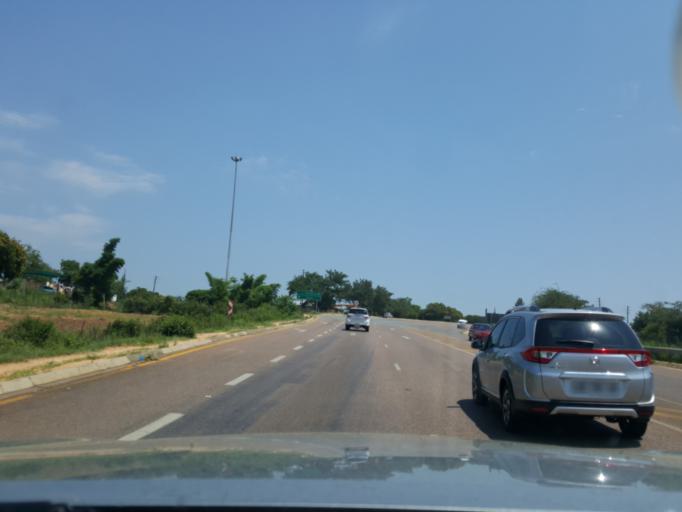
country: ZA
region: Limpopo
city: Thulamahashi
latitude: -24.9699
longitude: 31.1179
